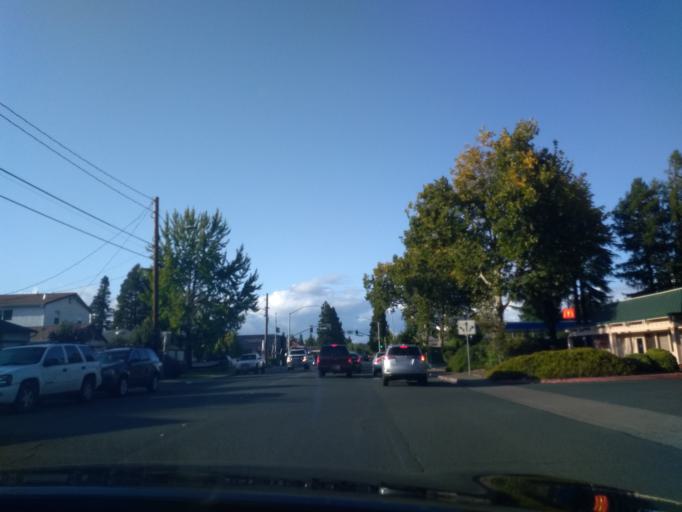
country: US
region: California
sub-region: Mendocino County
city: Ukiah
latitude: 39.1505
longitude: -123.1990
